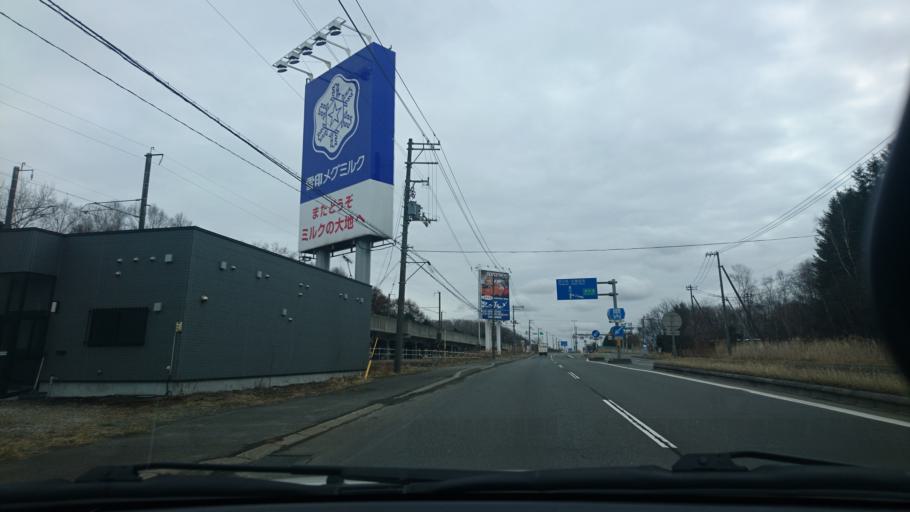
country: JP
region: Hokkaido
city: Chitose
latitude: 42.8202
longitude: 141.6606
